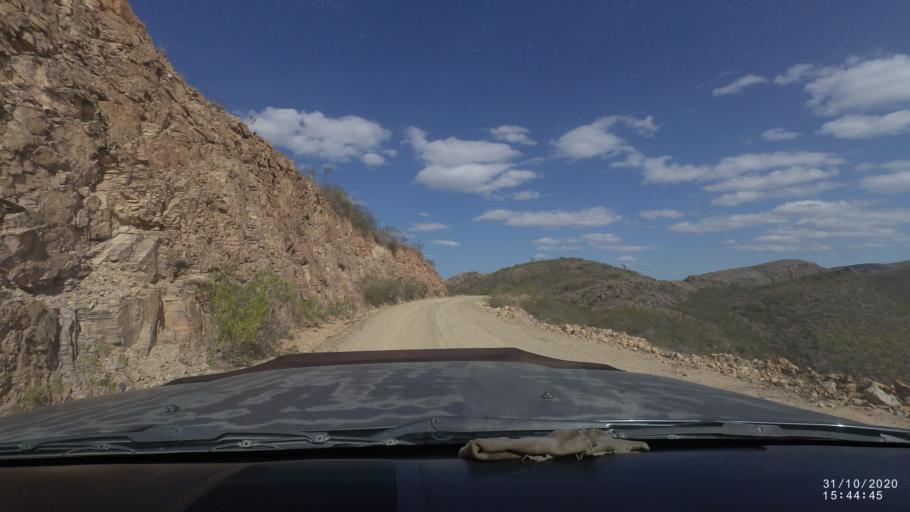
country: BO
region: Chuquisaca
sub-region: Provincia Zudanez
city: Mojocoya
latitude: -18.3178
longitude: -64.7216
